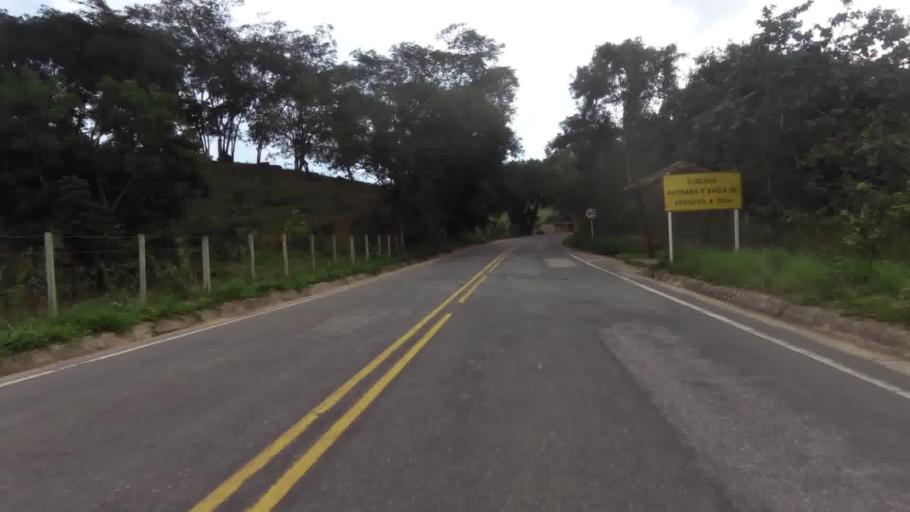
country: BR
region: Espirito Santo
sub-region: Alfredo Chaves
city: Alfredo Chaves
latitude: -20.6879
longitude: -40.7075
